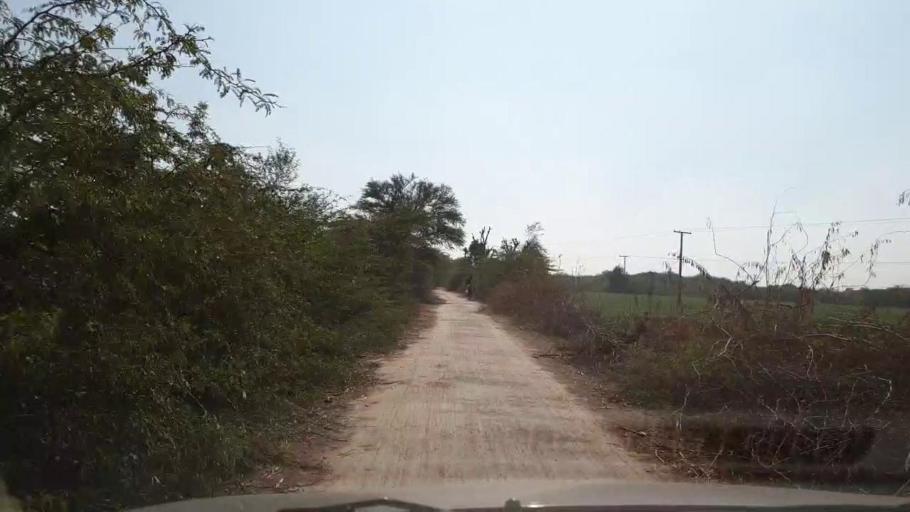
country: PK
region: Sindh
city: Jhol
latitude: 25.8904
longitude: 68.8291
